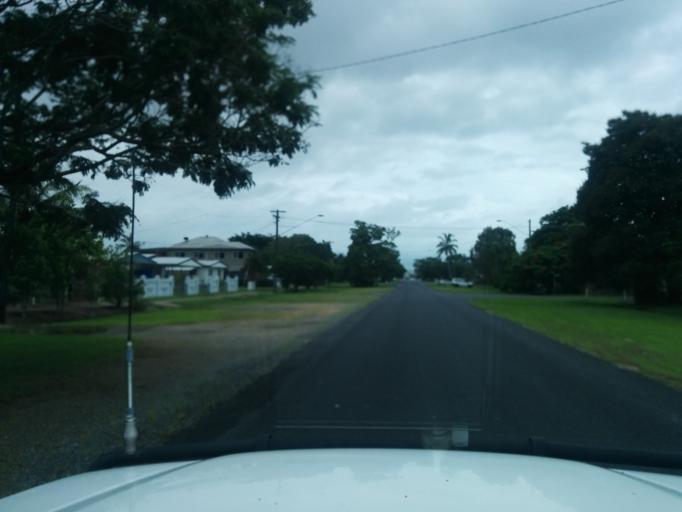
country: AU
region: Queensland
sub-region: Cairns
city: Cairns
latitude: -16.9320
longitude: 145.7544
